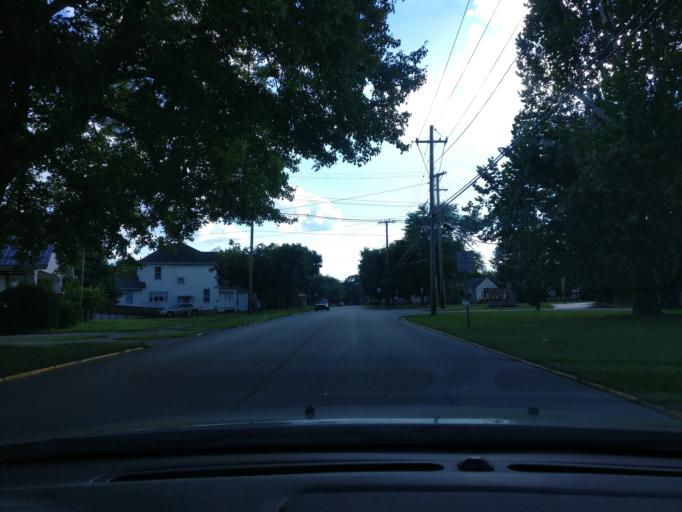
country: US
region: Ohio
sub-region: Clinton County
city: Wilmington
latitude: 39.4507
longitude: -83.8201
